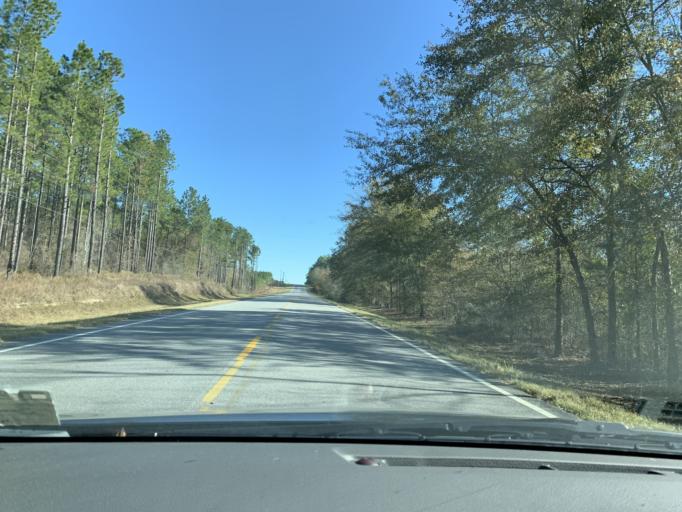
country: US
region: Georgia
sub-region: Ben Hill County
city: Fitzgerald
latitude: 31.7576
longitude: -83.1237
